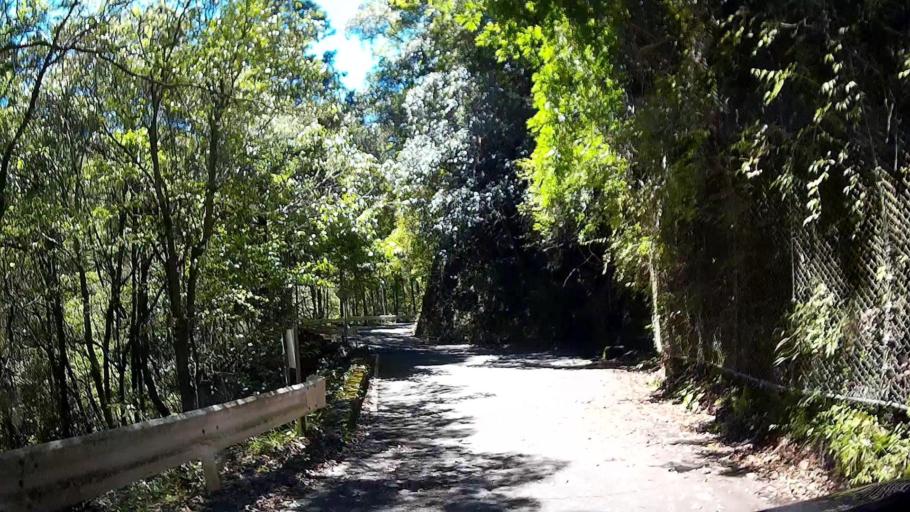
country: JP
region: Shizuoka
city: Shizuoka-shi
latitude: 35.1807
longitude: 138.2771
